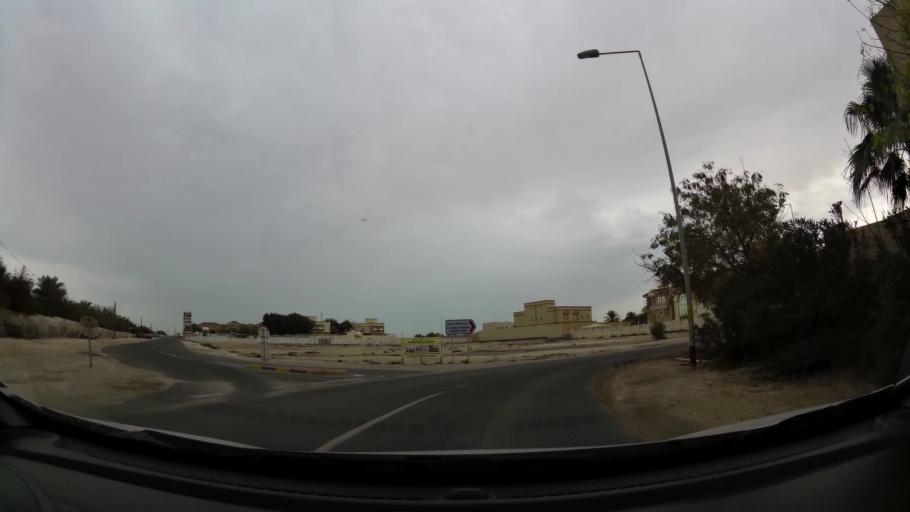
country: BH
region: Central Governorate
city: Madinat Hamad
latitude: 26.1505
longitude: 50.4710
